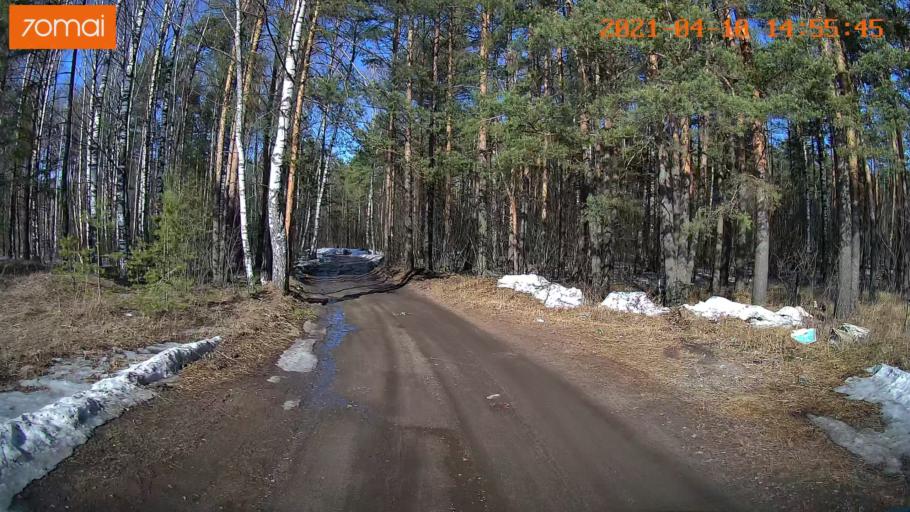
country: RU
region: Ivanovo
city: Kokhma
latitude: 56.9898
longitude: 41.0577
